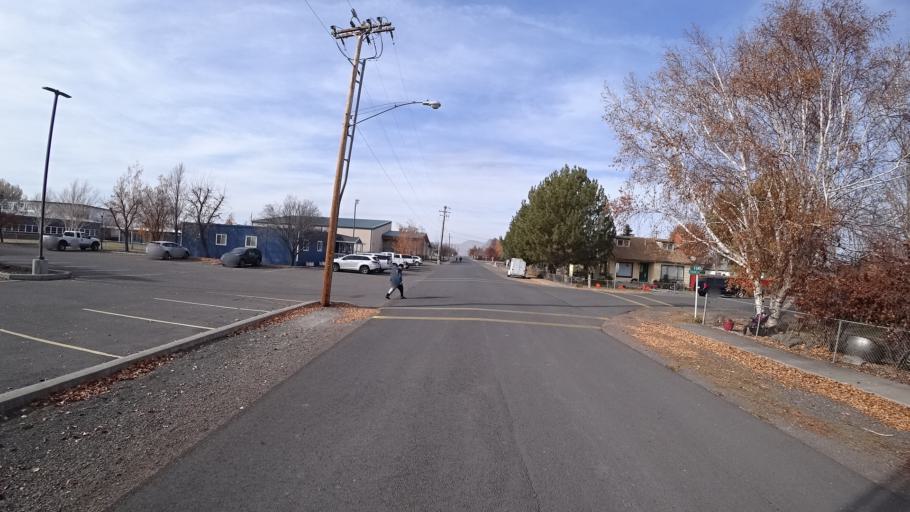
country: US
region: California
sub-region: Siskiyou County
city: Tulelake
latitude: 41.9510
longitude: -121.4750
